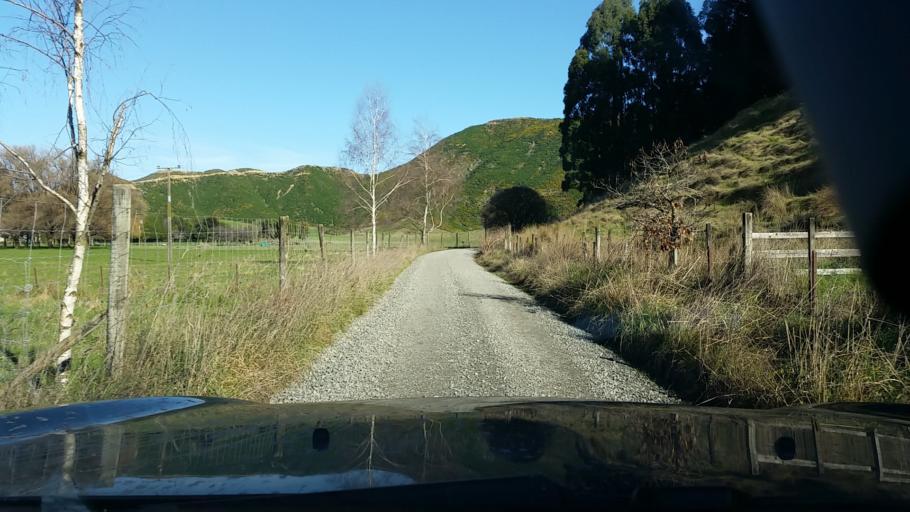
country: NZ
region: Marlborough
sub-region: Marlborough District
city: Blenheim
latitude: -41.4626
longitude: 173.7971
